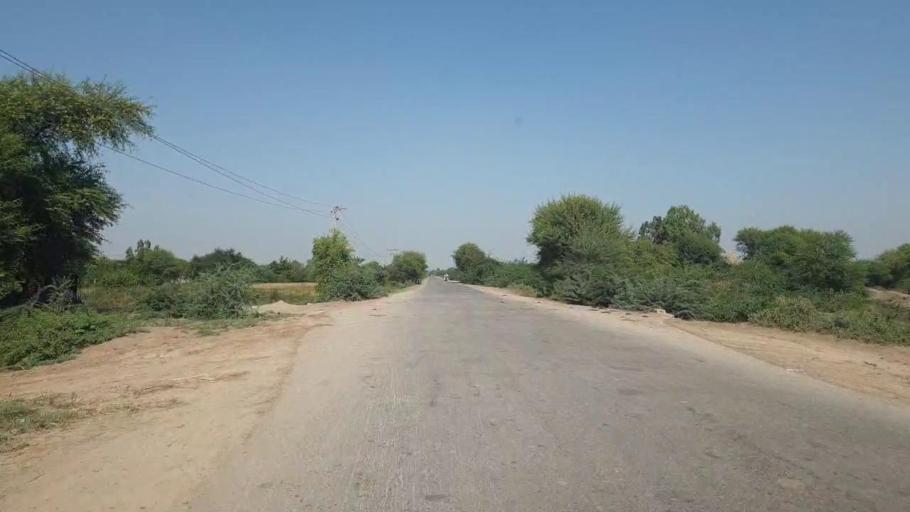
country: PK
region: Sindh
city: Talhar
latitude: 24.9137
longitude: 68.8579
